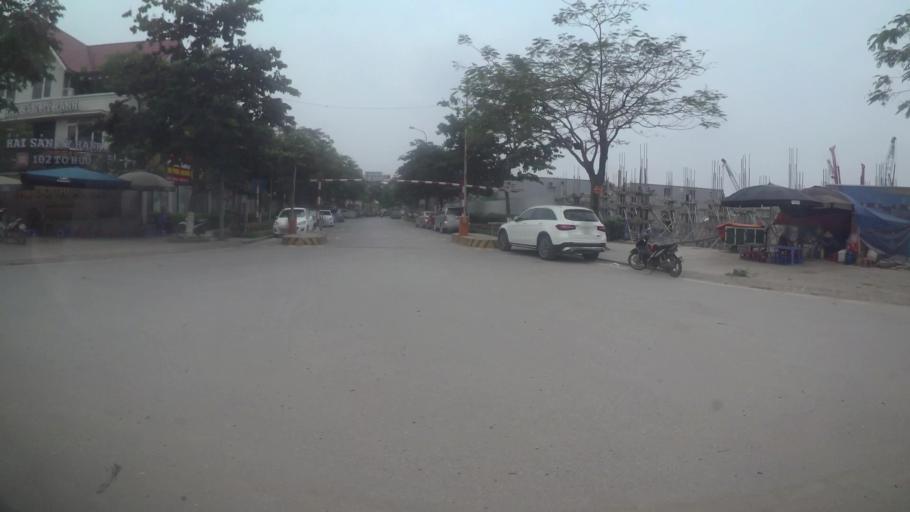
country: VN
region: Ha Noi
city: Ha Dong
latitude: 20.9718
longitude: 105.7559
